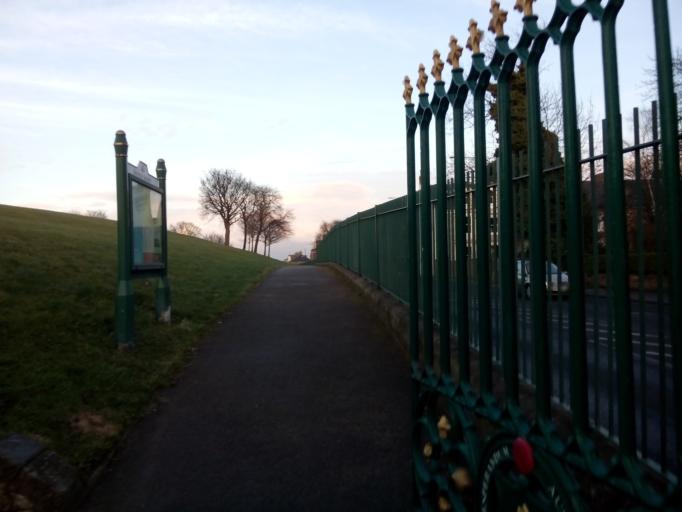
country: GB
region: England
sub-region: Sunderland
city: Sunderland
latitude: 54.9003
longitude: -1.3811
